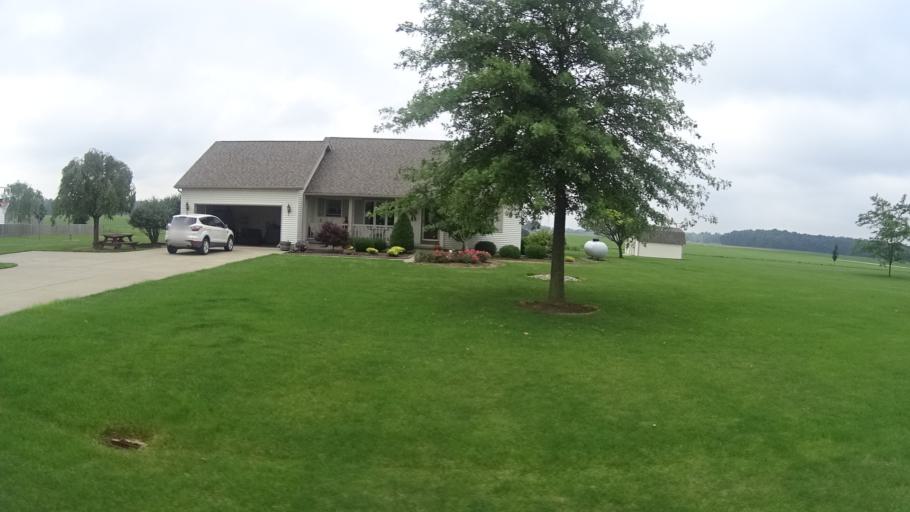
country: US
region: Ohio
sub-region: Erie County
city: Milan
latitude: 41.2801
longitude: -82.5069
